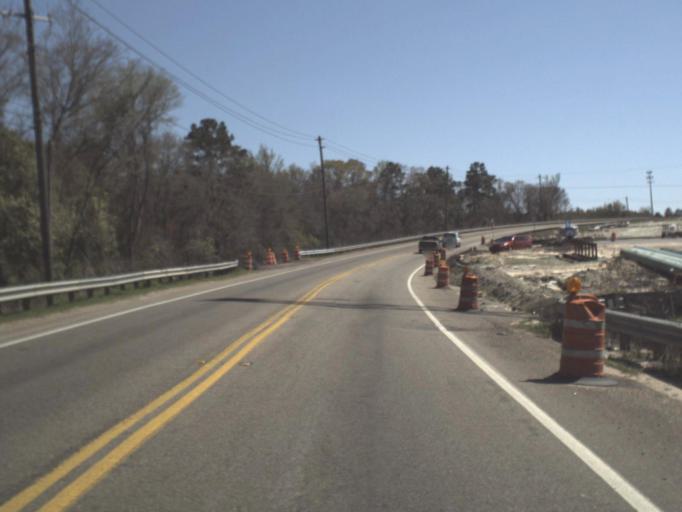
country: US
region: Florida
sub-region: Leon County
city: Tallahassee
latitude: 30.4451
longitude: -84.3541
